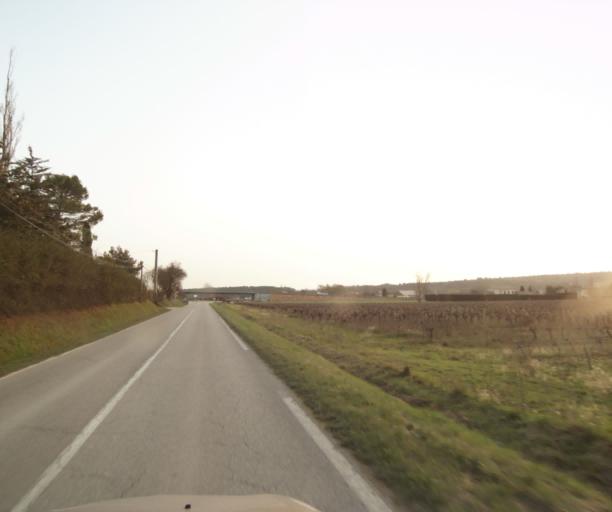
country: FR
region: Provence-Alpes-Cote d'Azur
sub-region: Departement des Bouches-du-Rhone
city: Eguilles
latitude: 43.5464
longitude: 5.3487
